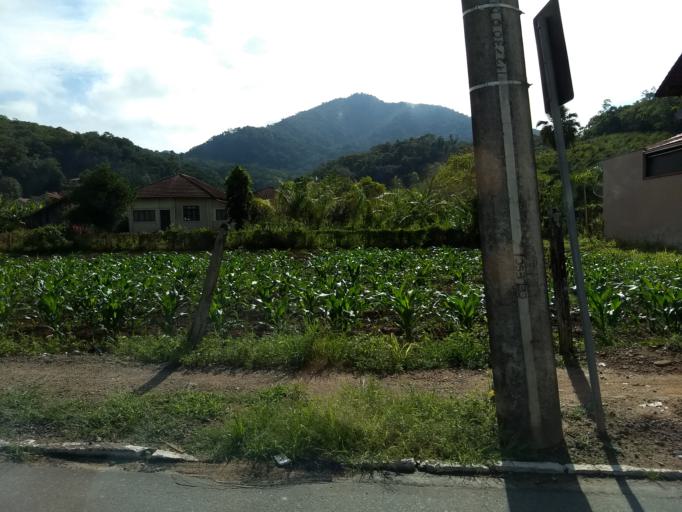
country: BR
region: Santa Catarina
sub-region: Jaragua Do Sul
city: Jaragua do Sul
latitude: -26.4588
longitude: -49.1049
